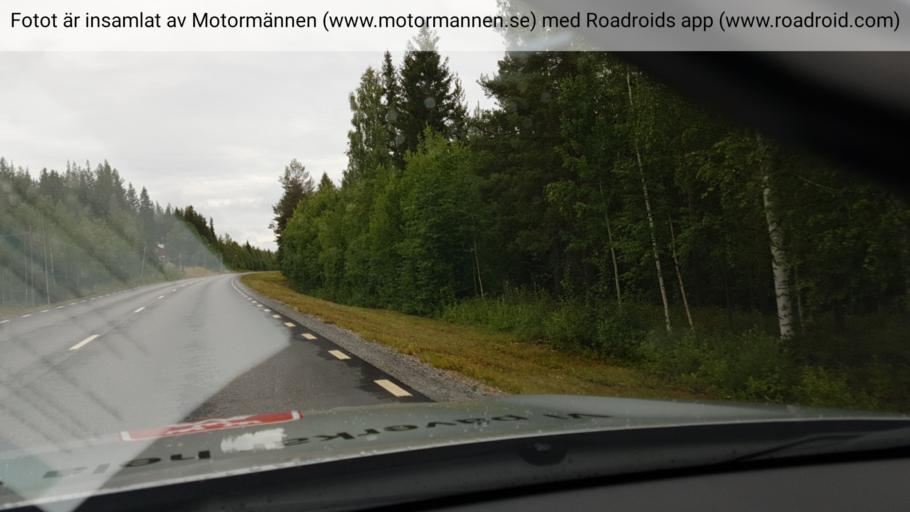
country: SE
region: Norrbotten
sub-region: Alvsbyns Kommun
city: AElvsbyn
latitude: 66.3033
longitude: 20.8032
